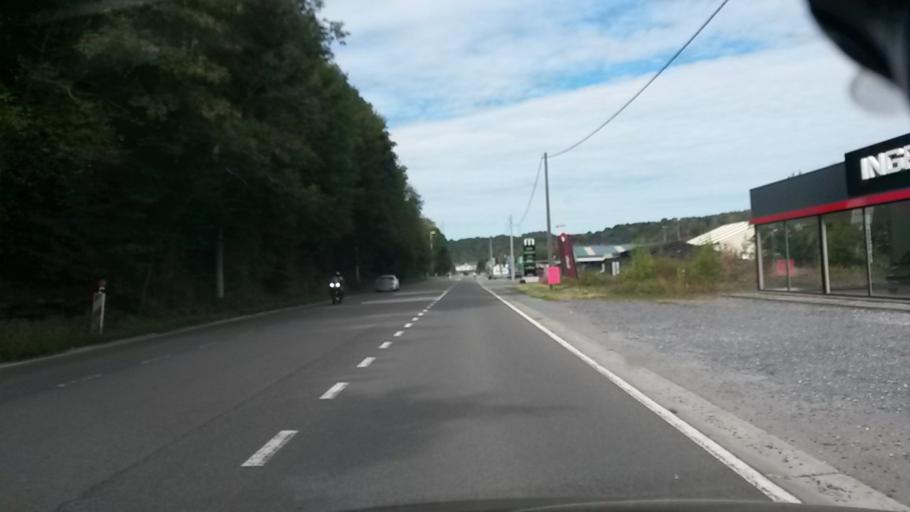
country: BE
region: Wallonia
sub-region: Province de Namur
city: Andenne
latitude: 50.4937
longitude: 5.0601
